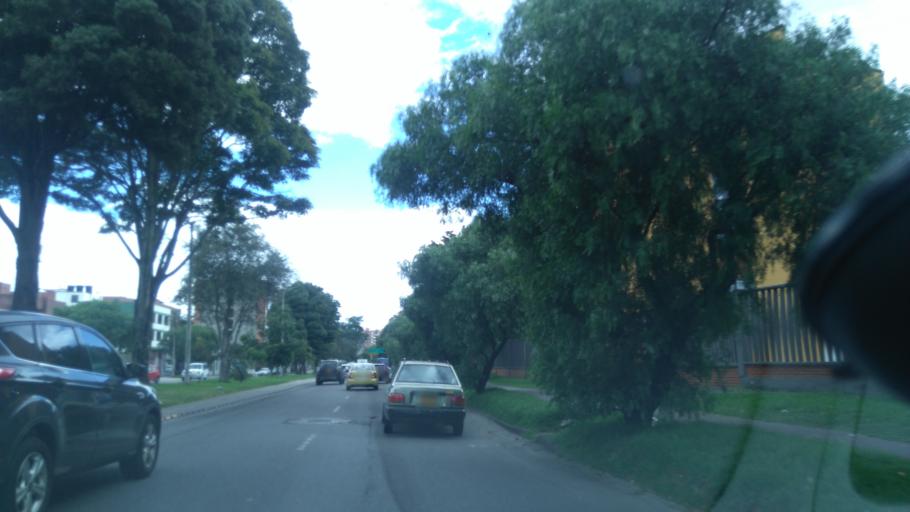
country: CO
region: Bogota D.C.
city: Bogota
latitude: 4.6504
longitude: -74.0849
